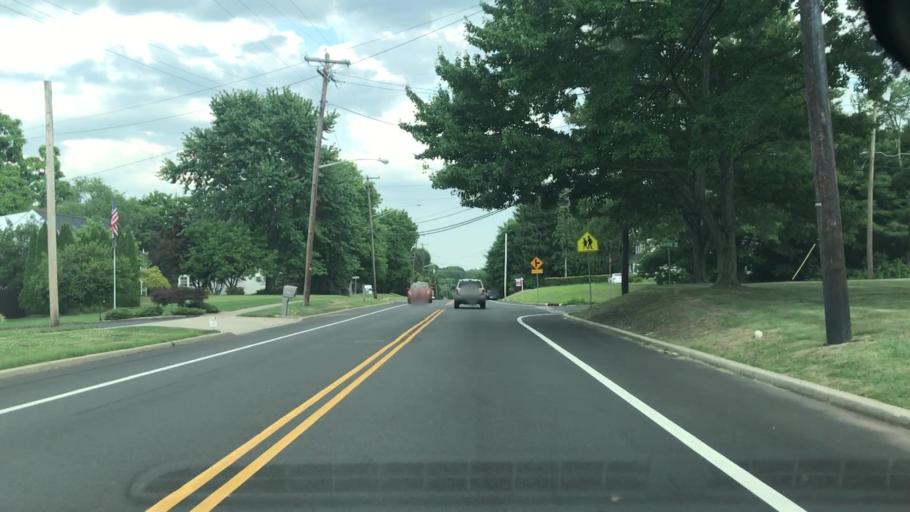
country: US
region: New Jersey
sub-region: Somerset County
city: Bradley Gardens
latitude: 40.5591
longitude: -74.6956
